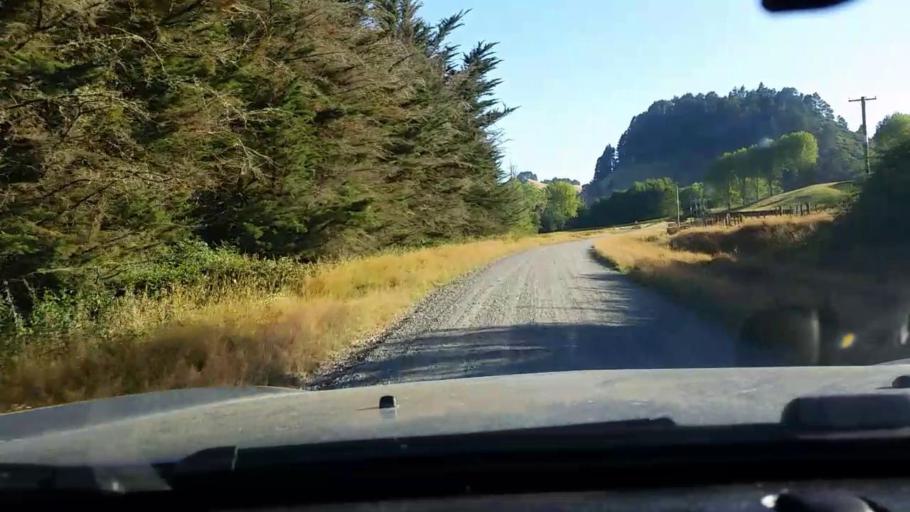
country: NZ
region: Waikato
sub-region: Taupo District
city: Taupo
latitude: -38.4591
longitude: 176.2412
